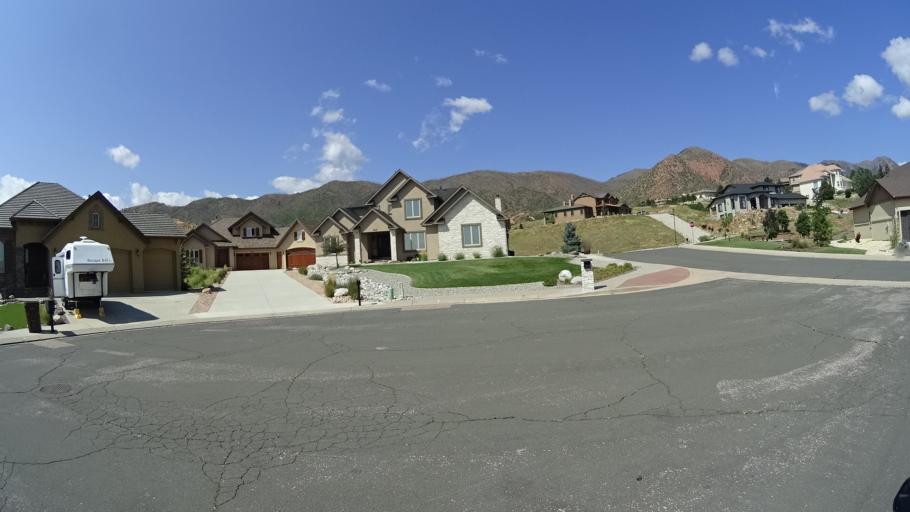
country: US
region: Colorado
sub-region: El Paso County
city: Manitou Springs
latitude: 38.9167
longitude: -104.8767
